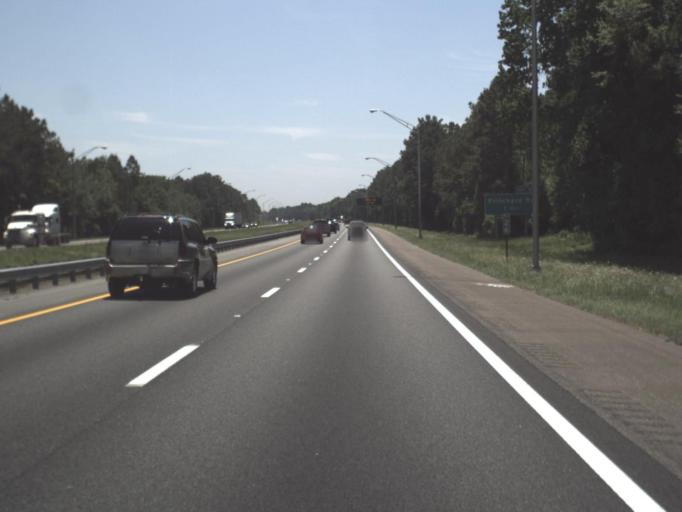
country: US
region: Florida
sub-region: Duval County
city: Jacksonville
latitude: 30.3912
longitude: -81.7583
